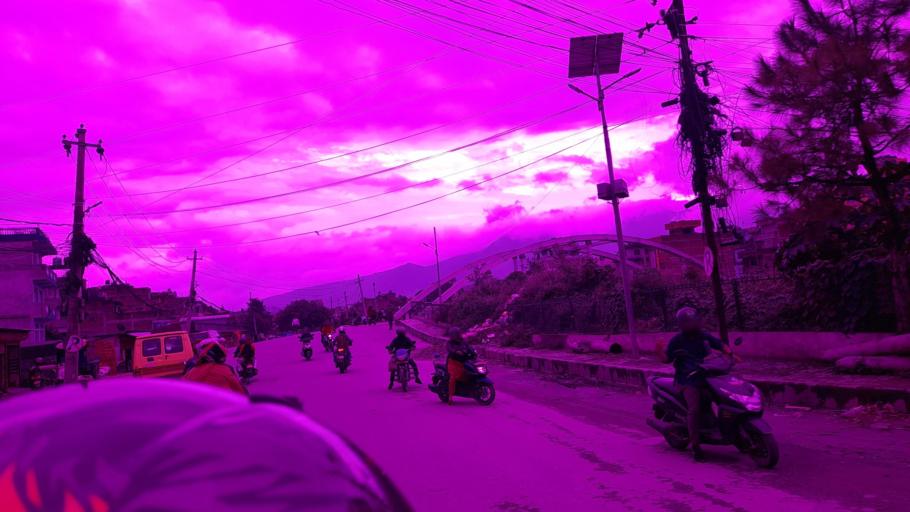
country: NP
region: Central Region
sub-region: Bagmati Zone
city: Kathmandu
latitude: 27.7094
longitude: 85.3032
